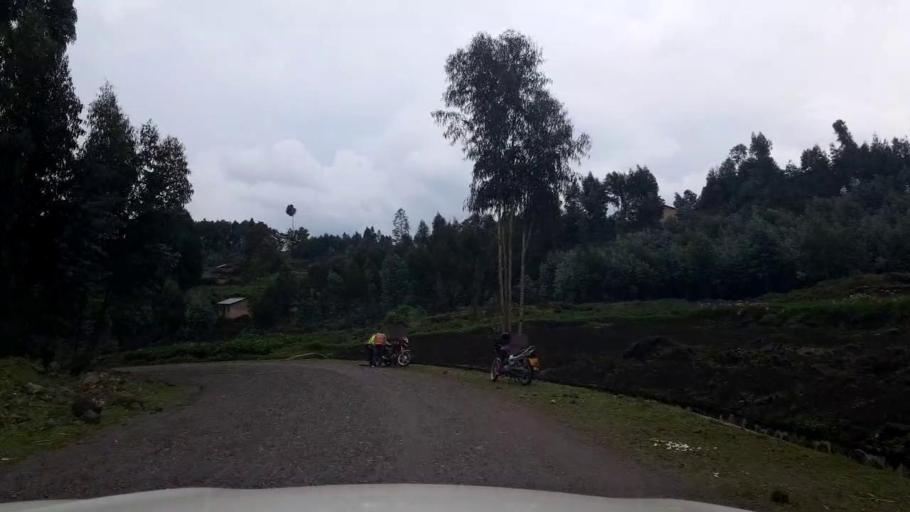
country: RW
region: Northern Province
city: Musanze
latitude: -1.5870
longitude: 29.4716
